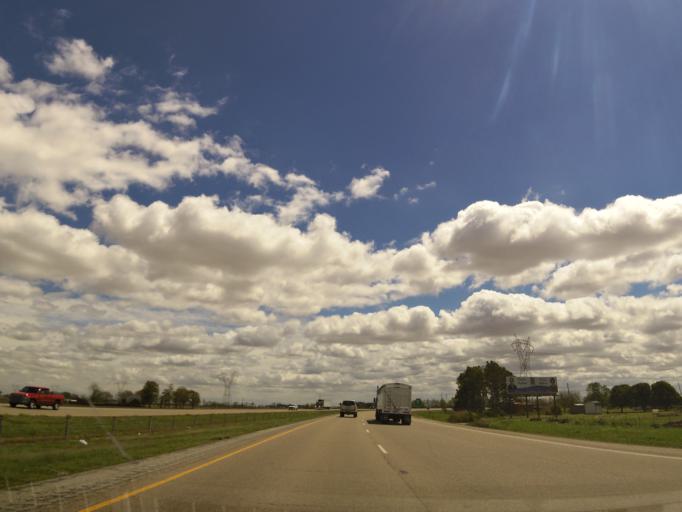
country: US
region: Arkansas
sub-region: Craighead County
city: Bay
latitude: 35.7724
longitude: -90.5814
